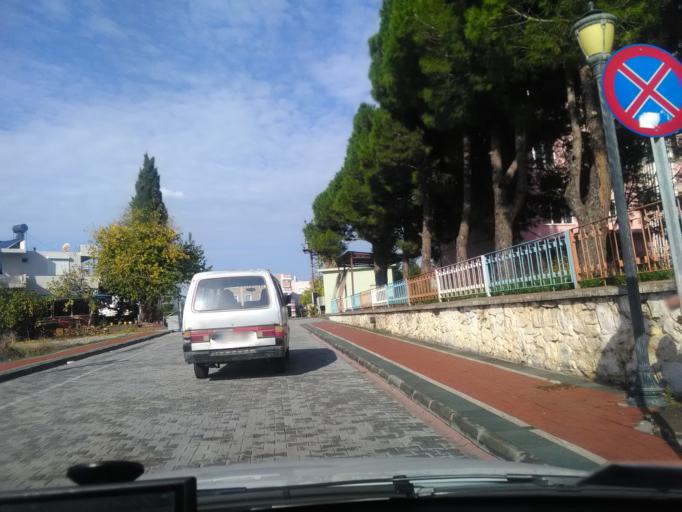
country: TR
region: Antalya
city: Gazipasa
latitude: 36.2708
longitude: 32.3087
